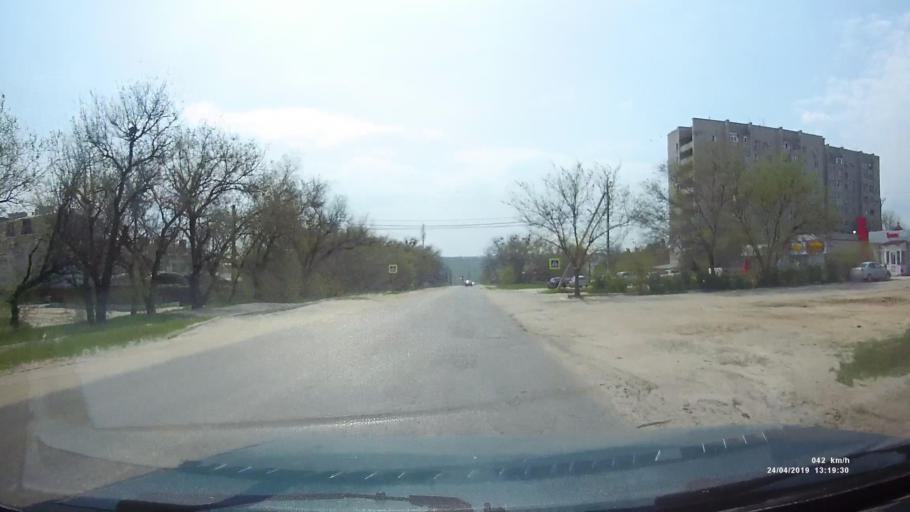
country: RU
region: Kalmykiya
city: Elista
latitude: 46.2997
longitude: 44.2904
